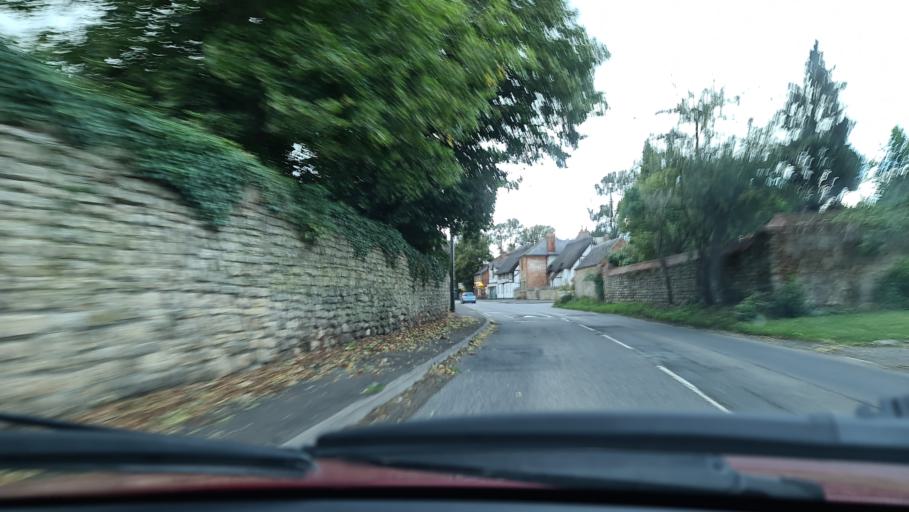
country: GB
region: England
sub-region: Buckinghamshire
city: Long Crendon
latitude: 51.7713
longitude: -0.9947
